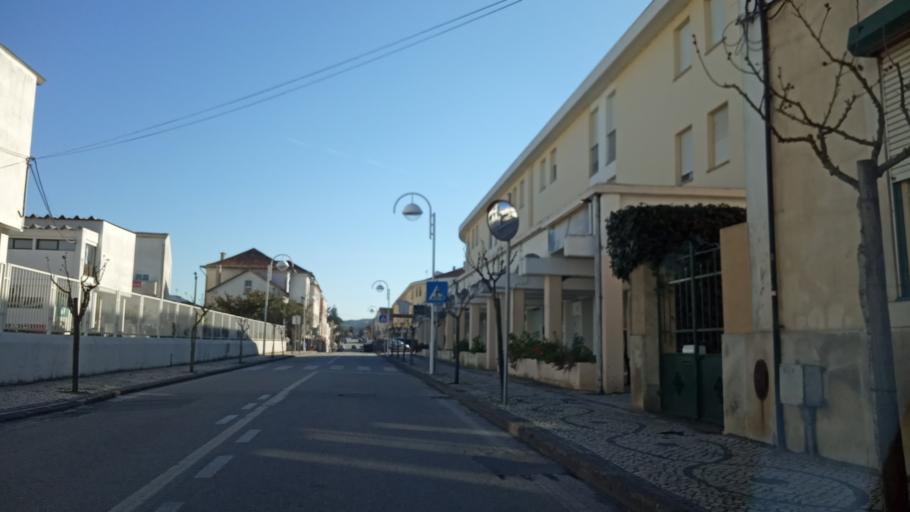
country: PT
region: Aveiro
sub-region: Anadia
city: Anadia
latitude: 40.4416
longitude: -8.4368
